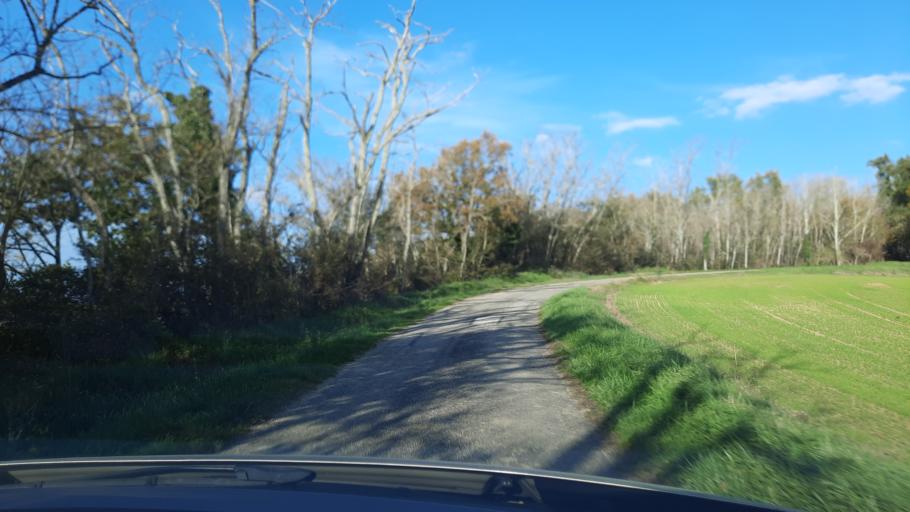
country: FR
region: Midi-Pyrenees
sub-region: Departement du Tarn-et-Garonne
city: Lafrancaise
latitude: 44.1767
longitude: 1.2825
